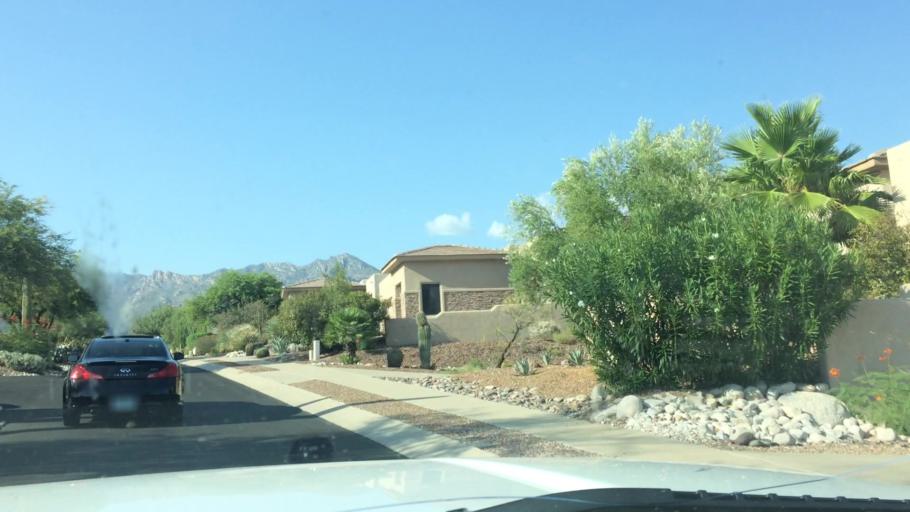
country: US
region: Arizona
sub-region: Pima County
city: Catalina Foothills
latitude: 32.2970
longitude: -110.8326
